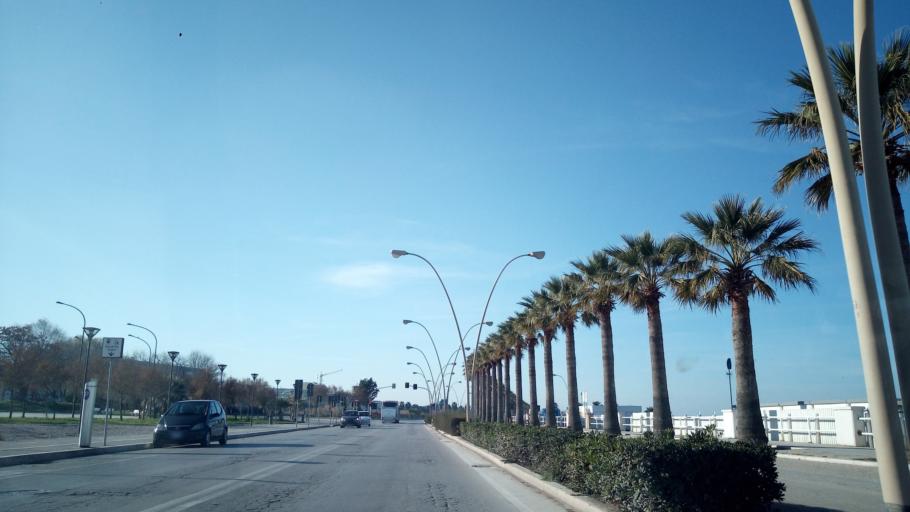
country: IT
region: Apulia
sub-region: Provincia di Barletta - Andria - Trani
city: Barletta
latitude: 41.3235
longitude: 16.2764
